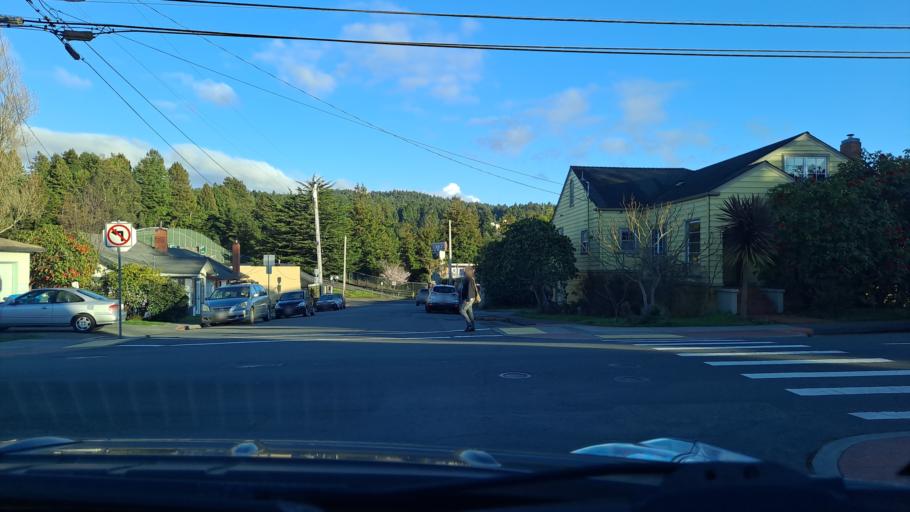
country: US
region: California
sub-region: Humboldt County
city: Arcata
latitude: 40.8754
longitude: -124.0846
